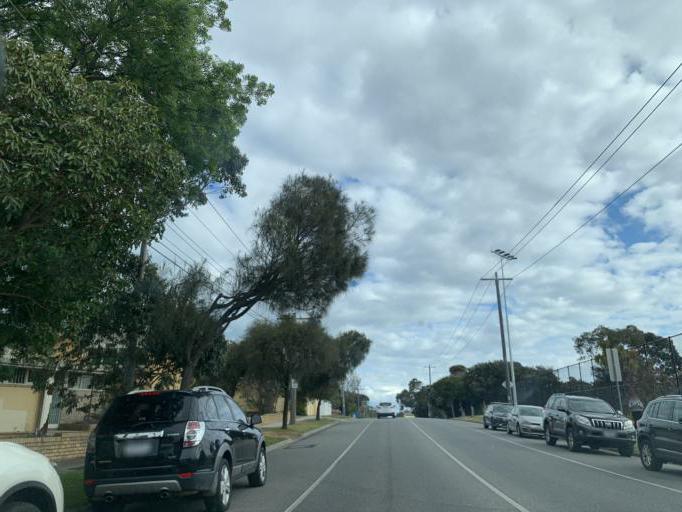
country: AU
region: Victoria
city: Beaumaris
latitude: -37.9791
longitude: 145.0342
